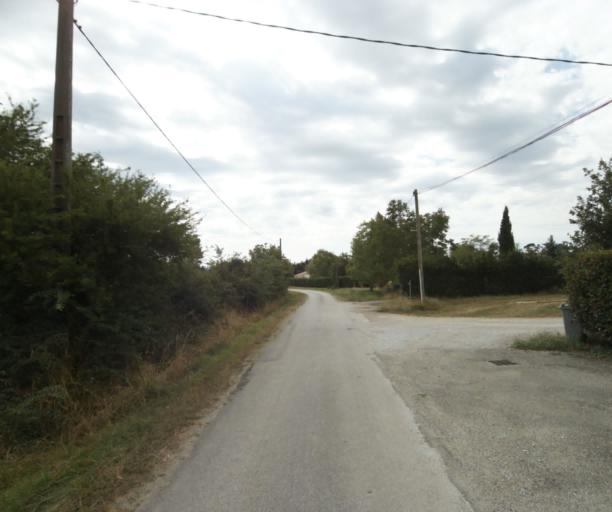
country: FR
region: Midi-Pyrenees
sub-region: Departement de la Haute-Garonne
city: Saint-Felix-Lauragais
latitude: 43.4328
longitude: 1.9400
